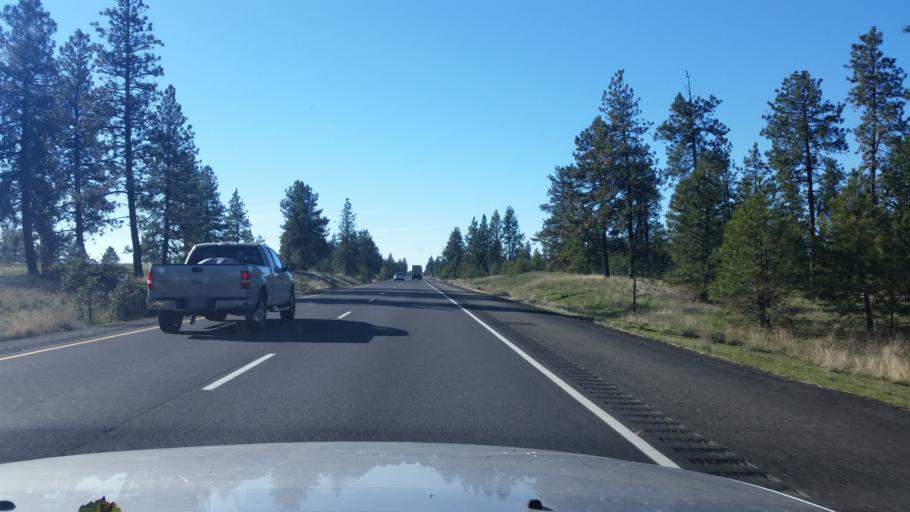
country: US
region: Washington
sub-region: Spokane County
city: Medical Lake
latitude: 47.4219
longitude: -117.8092
